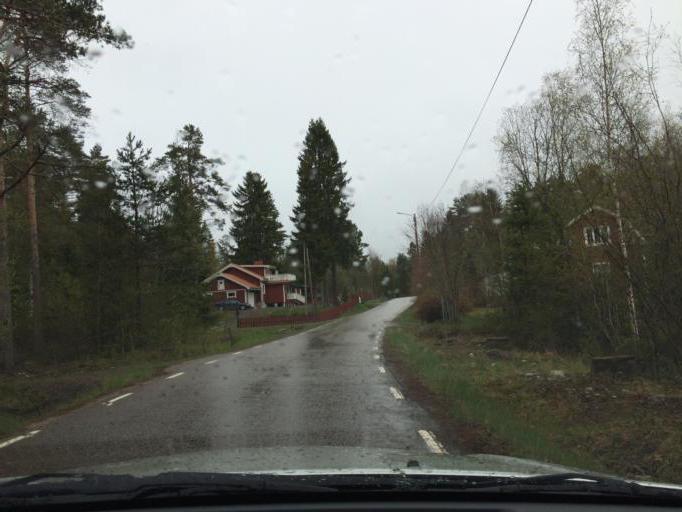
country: SE
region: Dalarna
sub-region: Ludvika Kommun
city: Abborrberget
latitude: 60.0446
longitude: 14.7662
